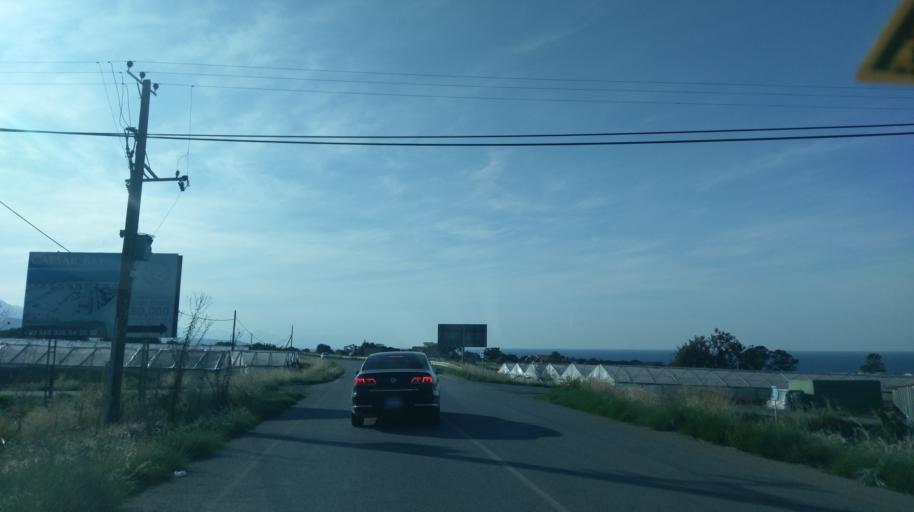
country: CY
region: Ammochostos
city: Lefkonoiko
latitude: 35.3725
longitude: 33.7087
